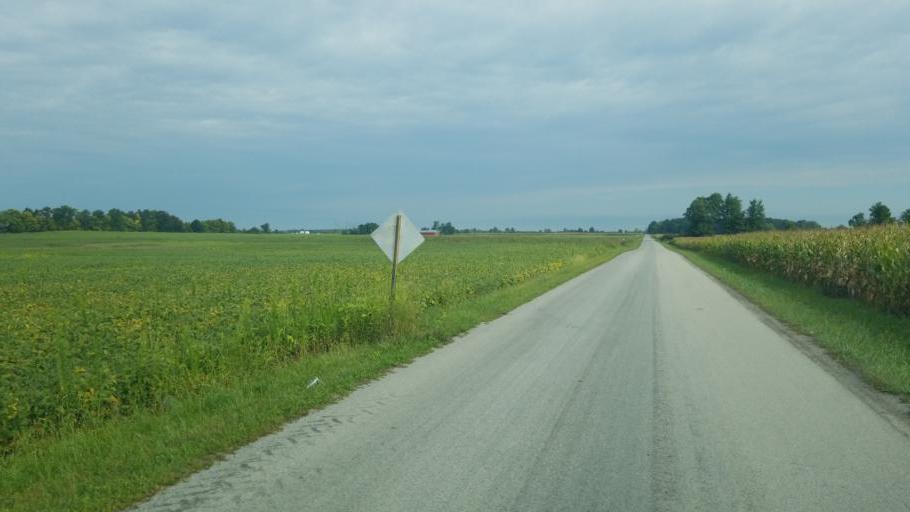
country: US
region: Ohio
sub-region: Marion County
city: Marion
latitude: 40.7161
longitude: -83.1305
